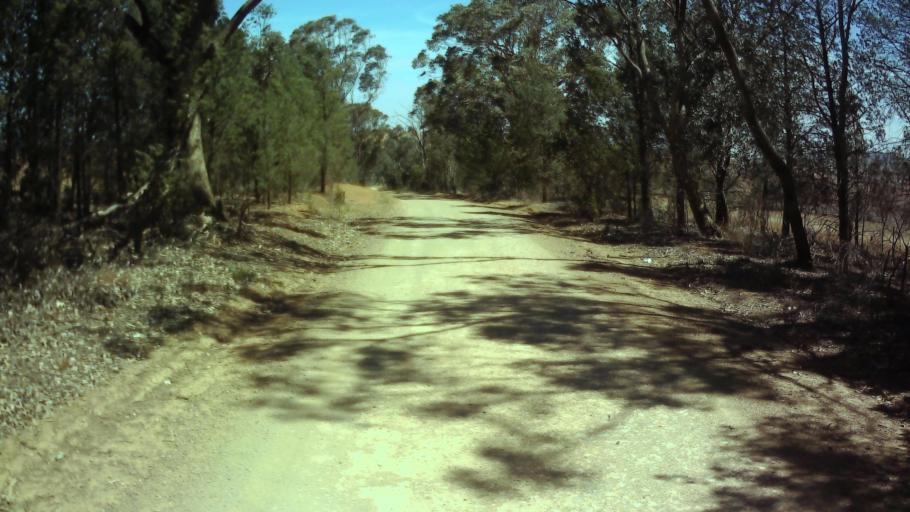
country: AU
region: New South Wales
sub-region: Weddin
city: Grenfell
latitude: -33.9188
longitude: 148.1790
